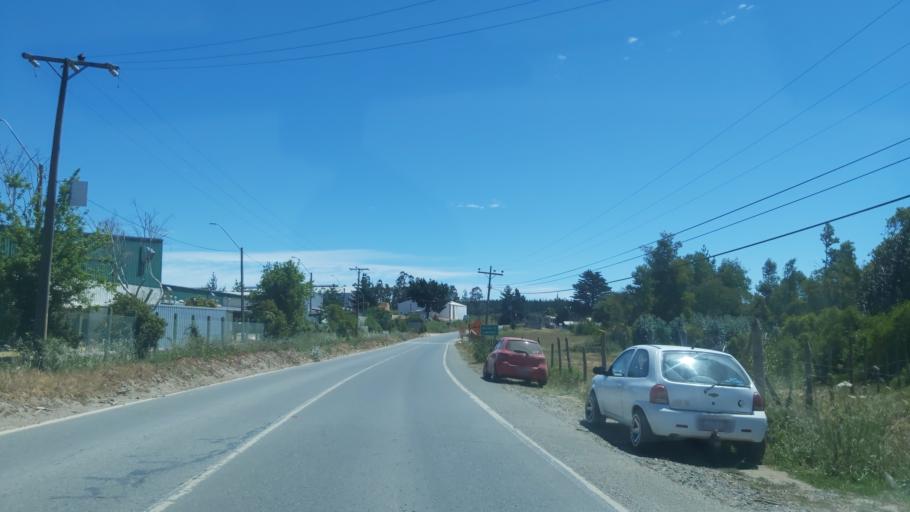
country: CL
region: Maule
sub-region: Provincia de Talca
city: Constitucion
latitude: -35.3742
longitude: -72.4161
